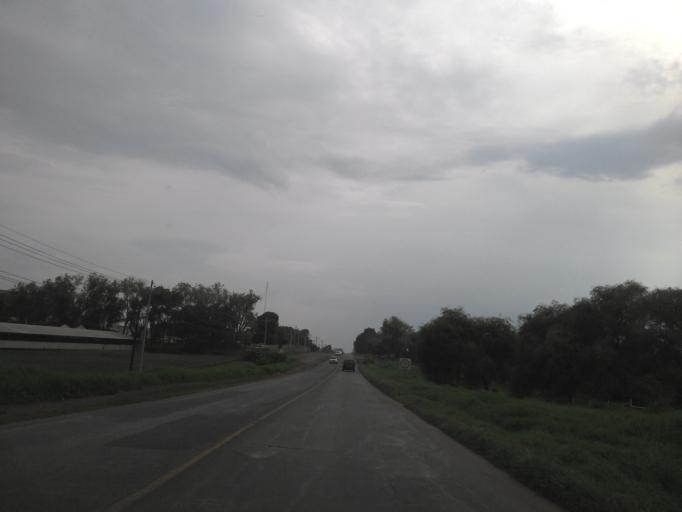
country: MX
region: Jalisco
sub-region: Acatic
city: Tierras Coloradas
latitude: 20.7587
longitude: -102.8219
